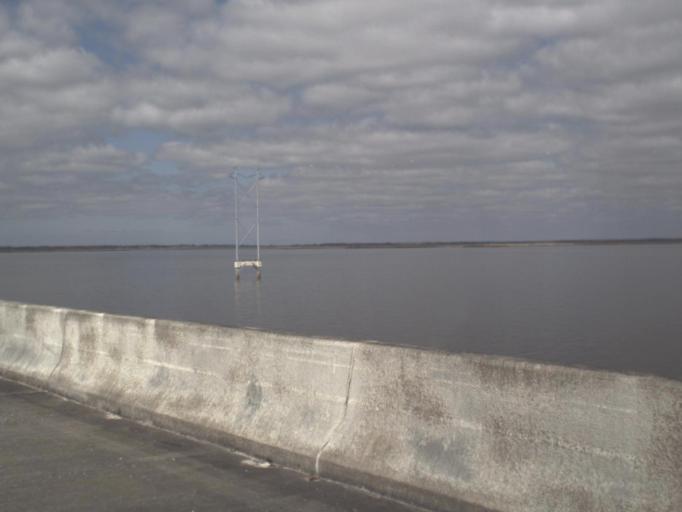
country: US
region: Florida
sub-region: Franklin County
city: Apalachicola
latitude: 29.7297
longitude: -84.9435
